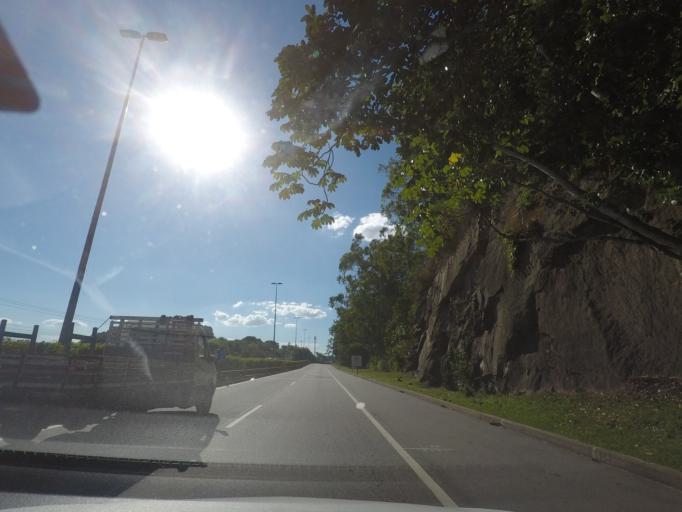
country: BR
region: Rio de Janeiro
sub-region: Sao Goncalo
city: Sao Goncalo
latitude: -22.6644
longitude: -43.1116
